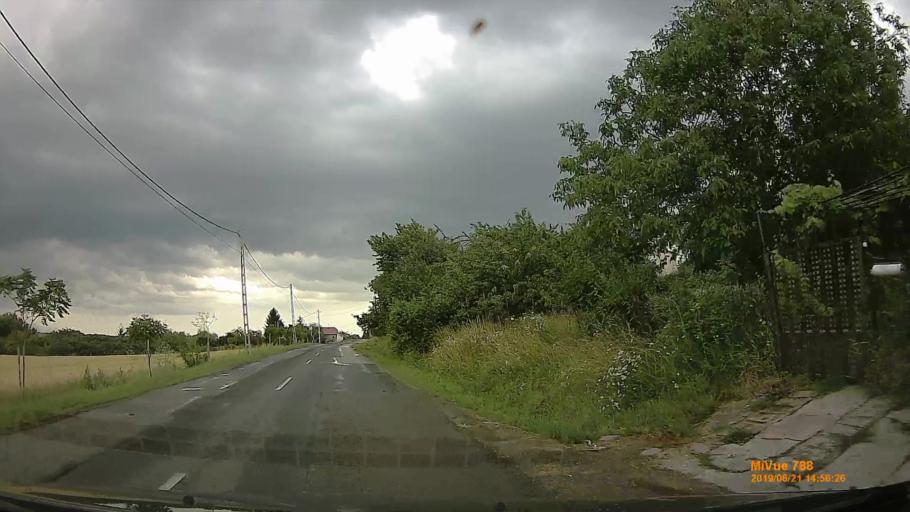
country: HU
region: Baranya
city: Hosszuheteny
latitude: 46.1152
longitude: 18.3121
